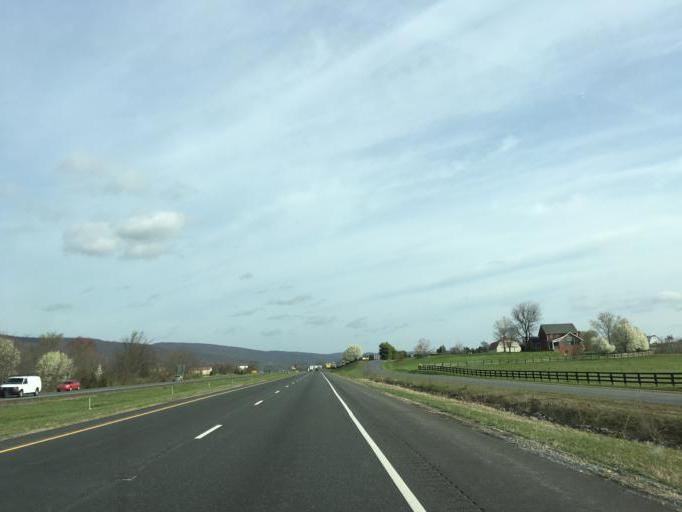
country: US
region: Maryland
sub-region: Frederick County
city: Clover Hill
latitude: 39.5388
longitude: -77.4245
